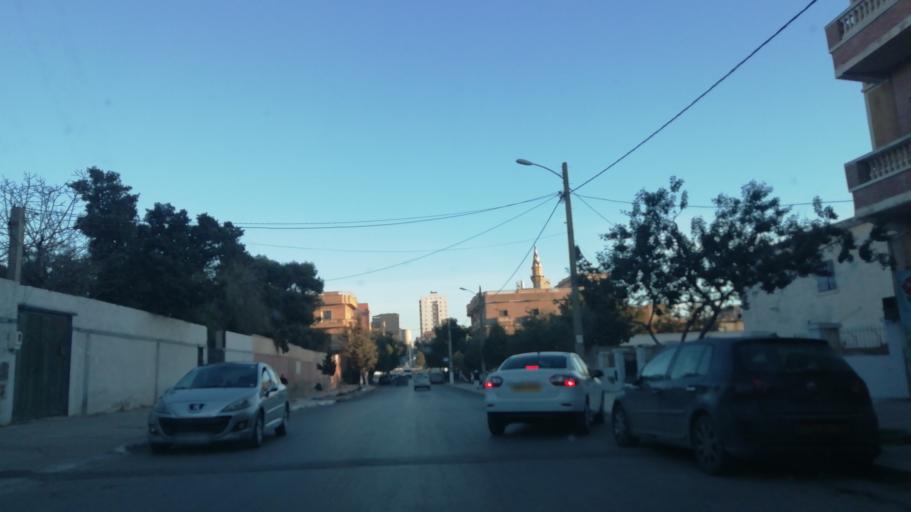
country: DZ
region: Oran
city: Bir el Djir
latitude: 35.7309
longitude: -0.5818
